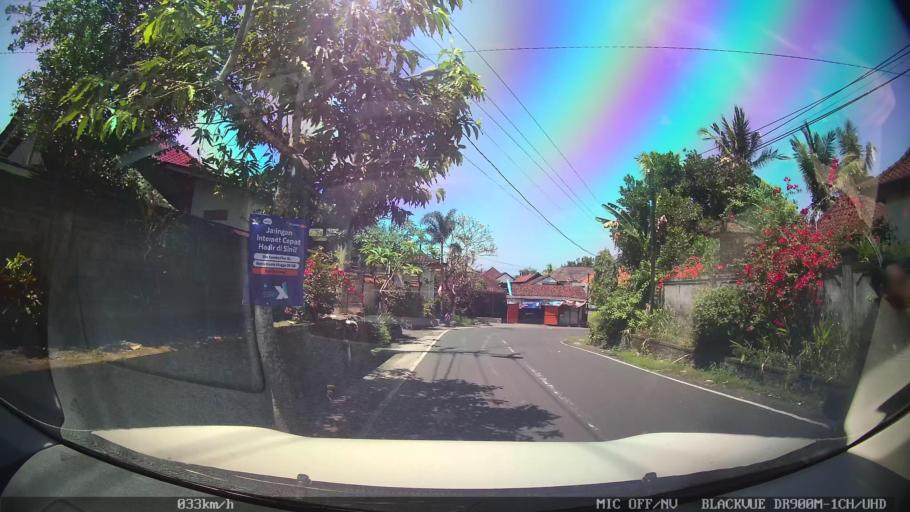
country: ID
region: Bali
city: Klungkung
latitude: -8.5708
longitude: 115.3357
